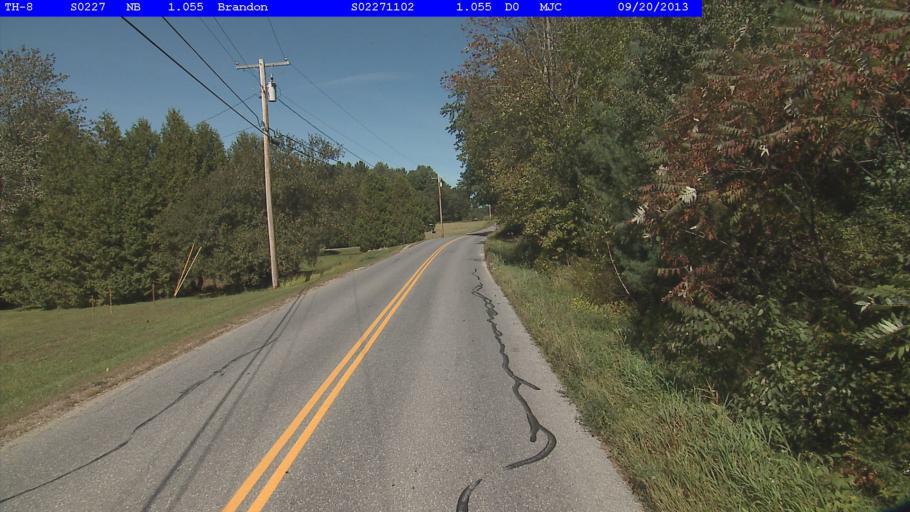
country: US
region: Vermont
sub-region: Rutland County
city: Brandon
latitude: 43.7896
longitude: -73.0539
